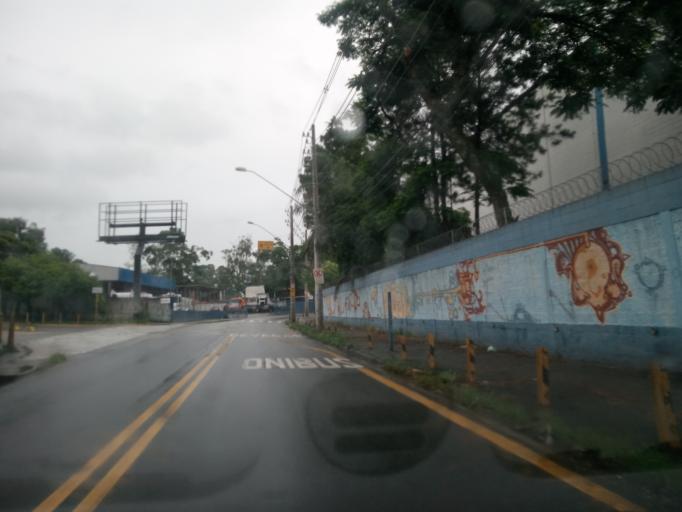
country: BR
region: Sao Paulo
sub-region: Sao Bernardo Do Campo
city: Sao Bernardo do Campo
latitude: -23.7443
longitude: -46.5549
